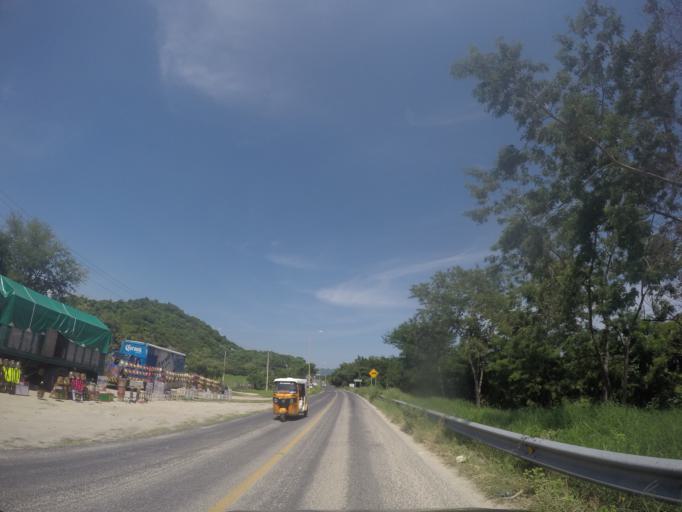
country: MX
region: Oaxaca
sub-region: Villa de Tututepec de Melchor Ocampo
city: Santa Rosa de Lima
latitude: 16.0105
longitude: -97.4512
